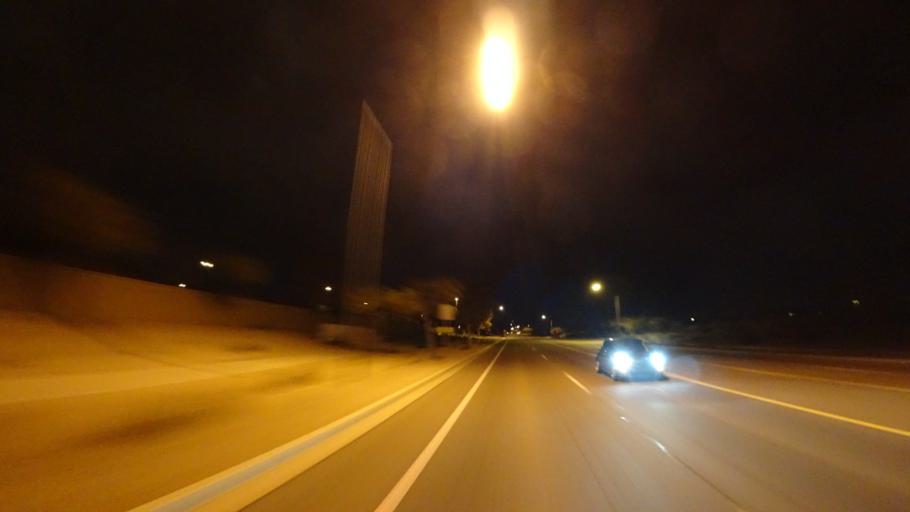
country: US
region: Arizona
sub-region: Maricopa County
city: Queen Creek
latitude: 33.2638
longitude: -111.7087
